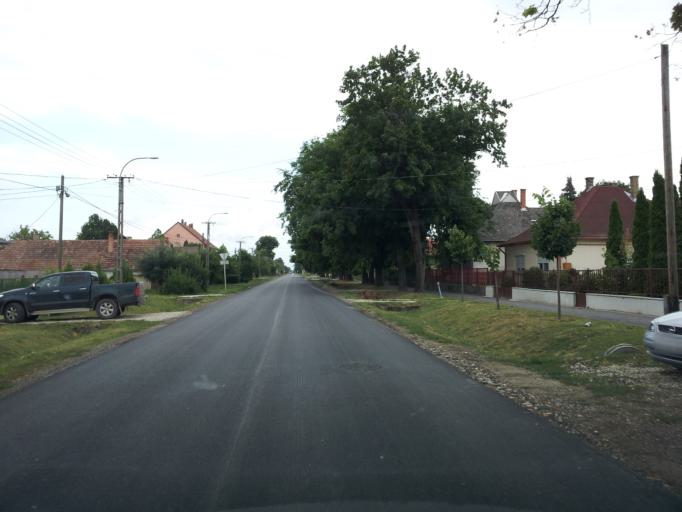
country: HU
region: Fejer
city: Enying
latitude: 46.9234
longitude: 18.2469
